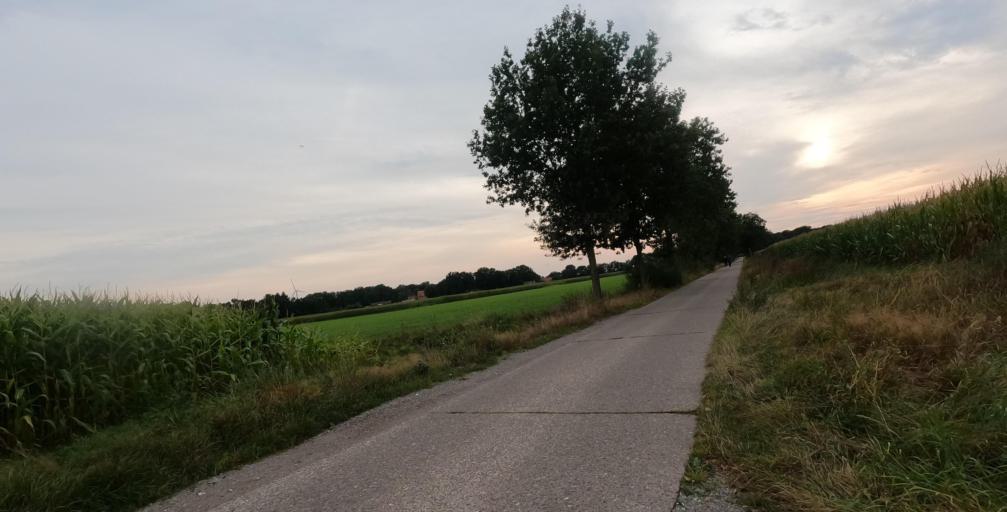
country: BE
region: Flanders
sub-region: Provincie Antwerpen
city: Essen
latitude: 51.4607
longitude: 4.5142
